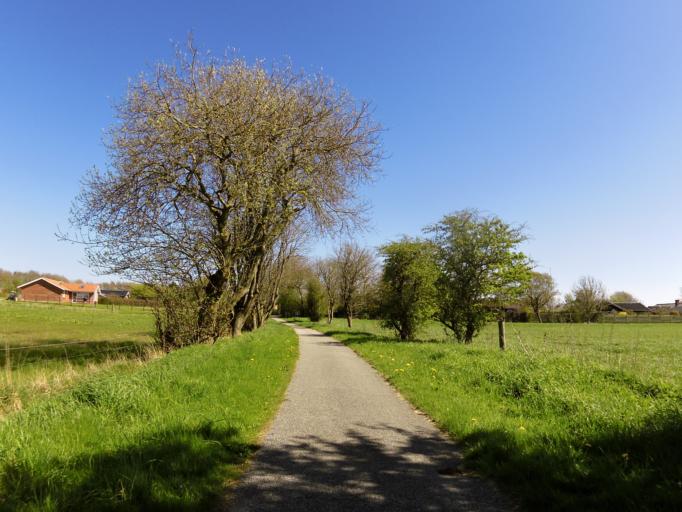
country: DK
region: Central Jutland
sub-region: Holstebro Kommune
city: Vinderup
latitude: 56.5947
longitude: 8.7802
